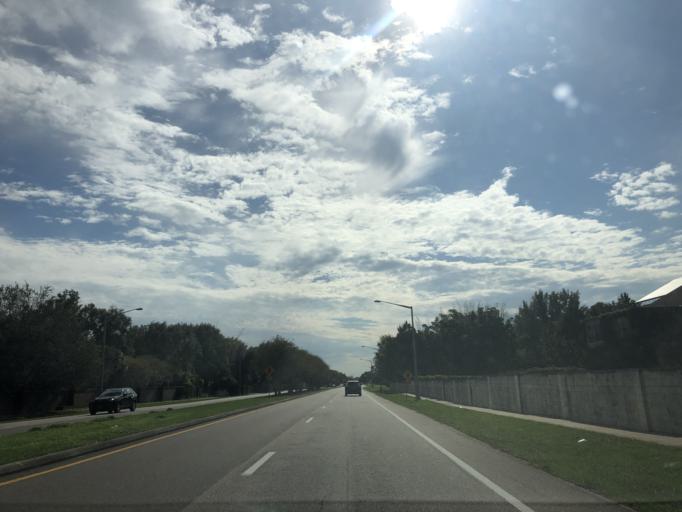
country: US
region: Florida
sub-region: Orange County
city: Bay Hill
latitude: 28.4764
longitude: -81.4916
